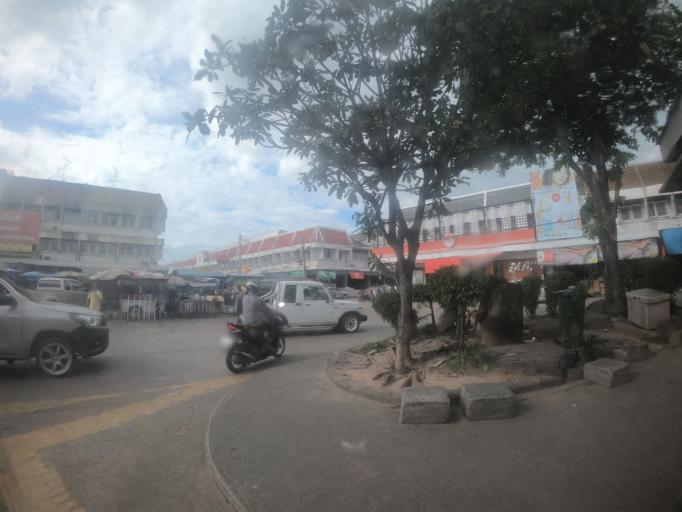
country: TH
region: Surin
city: Prasat
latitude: 14.6369
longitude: 103.4080
